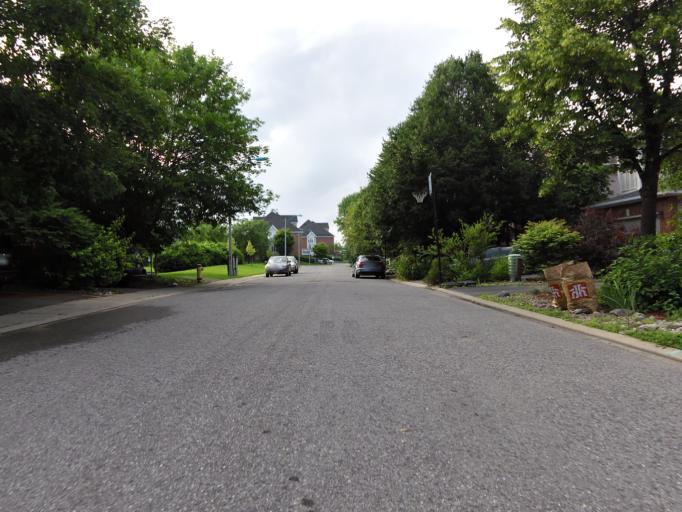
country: CA
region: Ontario
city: Bells Corners
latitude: 45.3200
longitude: -75.8917
